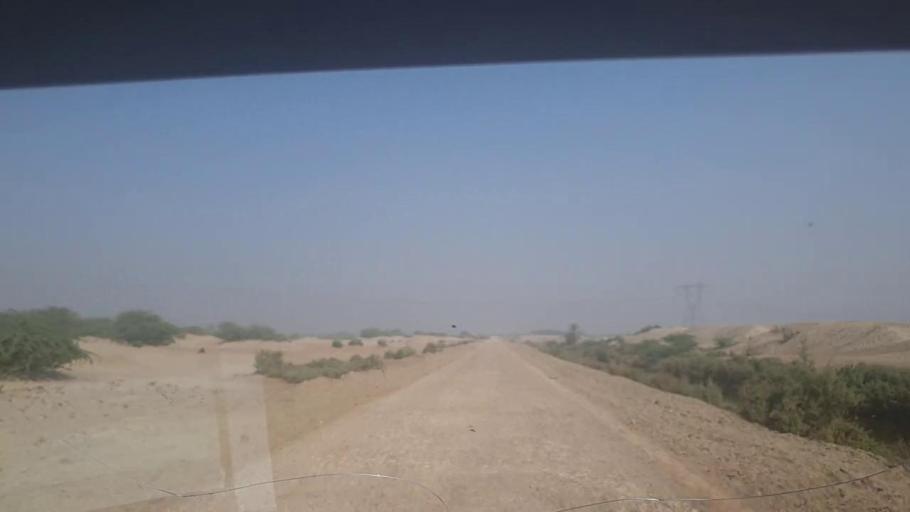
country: PK
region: Sindh
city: Khairpur
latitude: 27.4455
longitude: 68.7176
